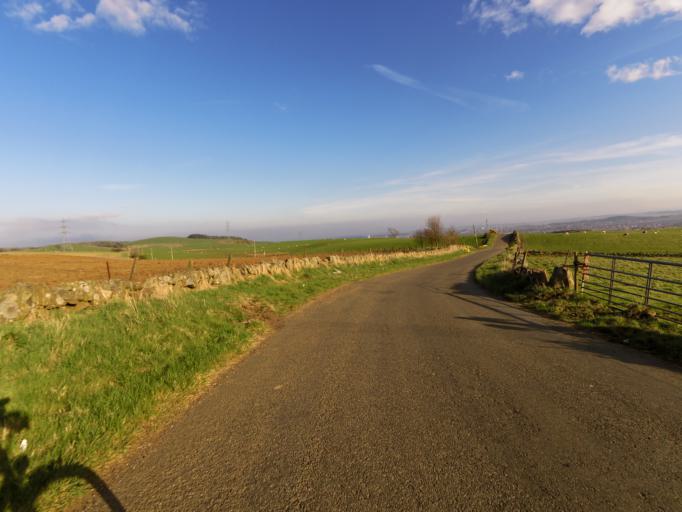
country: GB
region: Scotland
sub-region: Fife
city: Leslie
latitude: 56.2228
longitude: -3.2198
